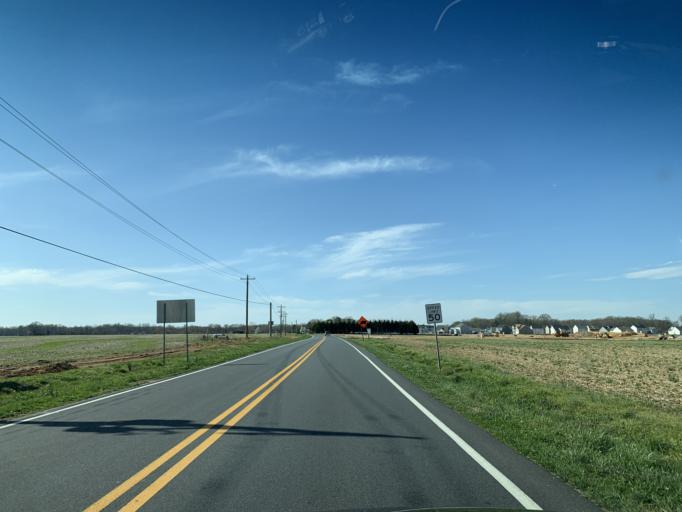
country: US
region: Delaware
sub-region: Kent County
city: Riverview
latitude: 38.9789
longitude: -75.5010
